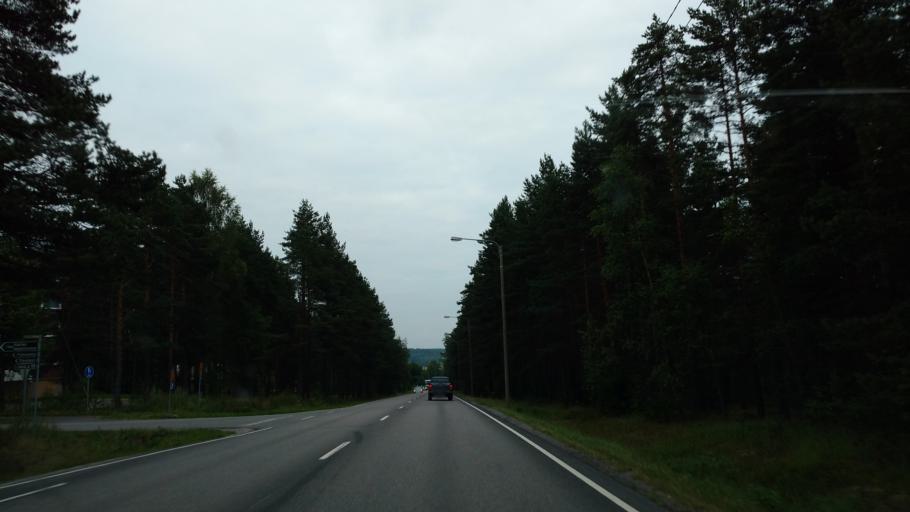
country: FI
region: Varsinais-Suomi
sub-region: Salo
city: Halikko
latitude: 60.4392
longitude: 23.0416
